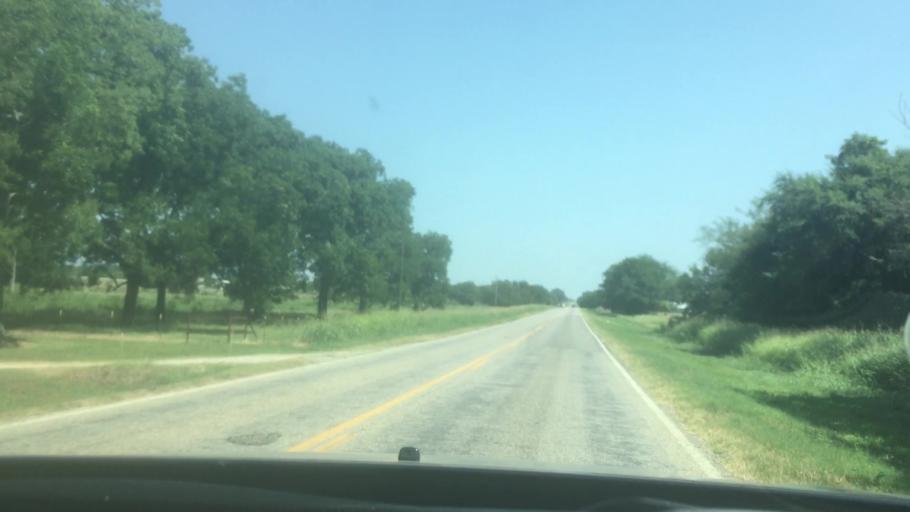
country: US
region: Oklahoma
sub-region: Johnston County
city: Tishomingo
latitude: 34.2884
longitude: -96.4248
